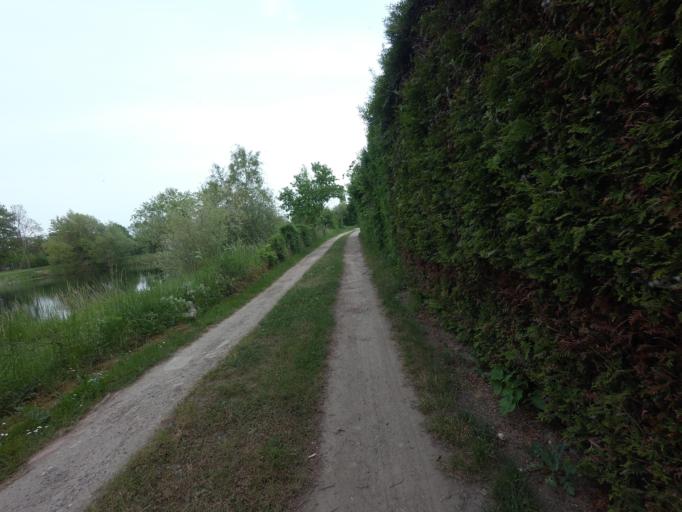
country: DE
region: Lower Saxony
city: Nordstemmen
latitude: 52.1584
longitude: 9.7576
